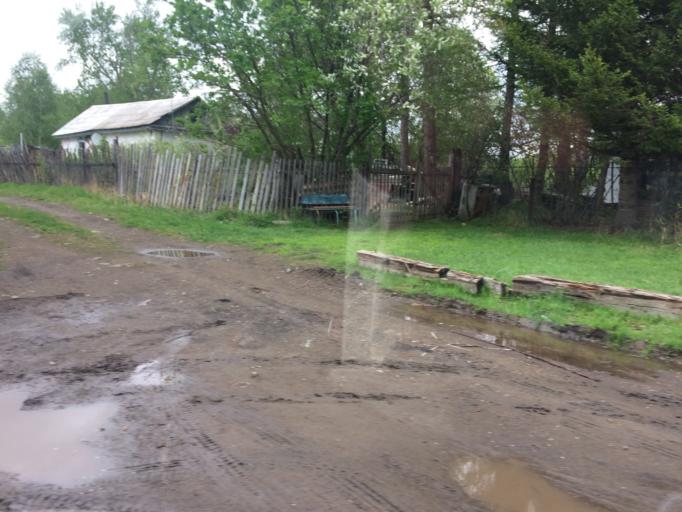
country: RU
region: Bashkortostan
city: Abzakovo
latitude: 53.6072
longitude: 58.6310
